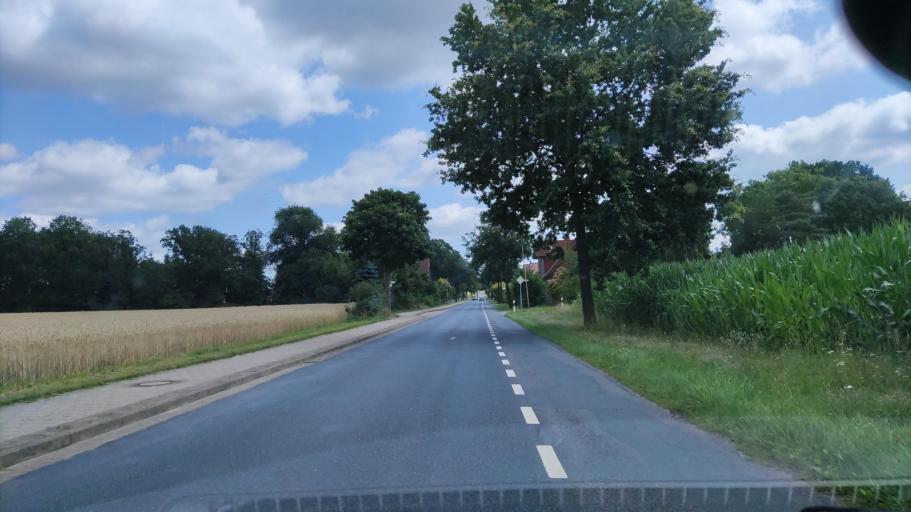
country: DE
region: Lower Saxony
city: Walsrode
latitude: 52.8305
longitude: 9.6429
